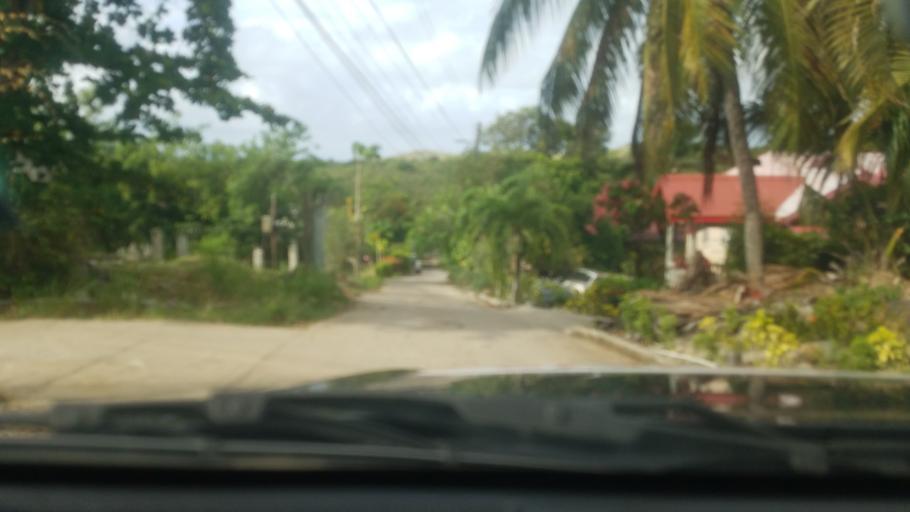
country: LC
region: Micoud Quarter
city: Micoud
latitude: 13.7943
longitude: -60.9117
